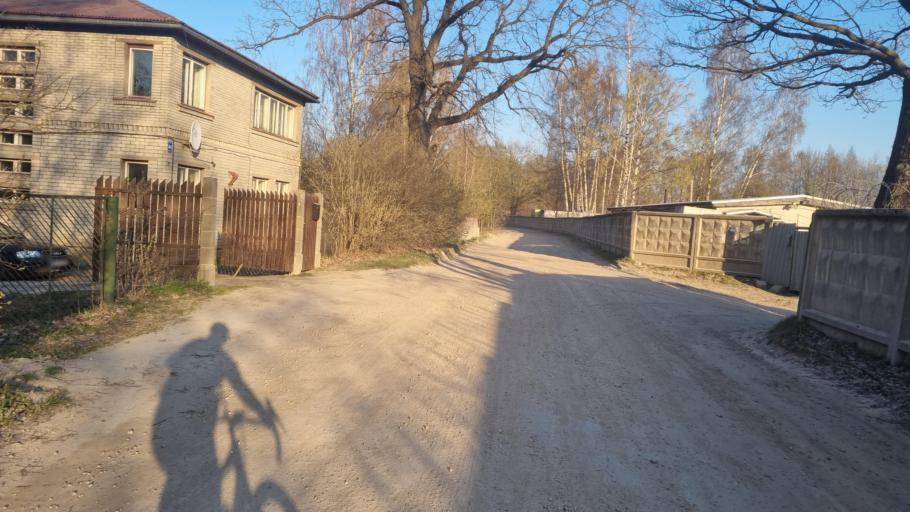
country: LV
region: Kekava
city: Balozi
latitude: 56.9093
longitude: 24.1176
